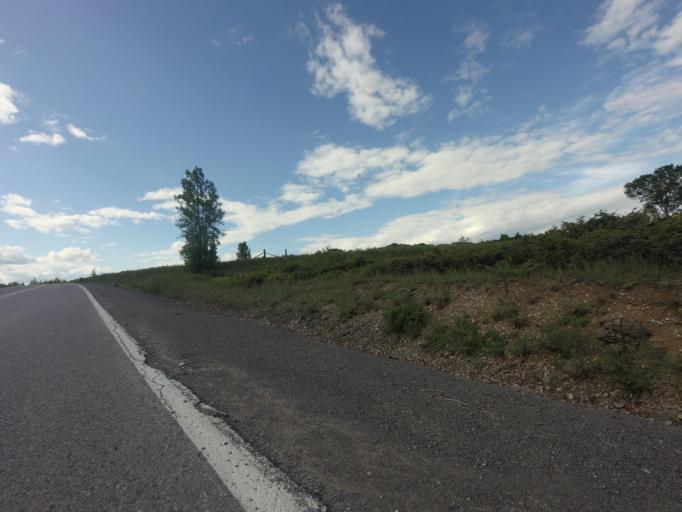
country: CA
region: Ontario
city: Arnprior
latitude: 45.3392
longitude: -76.1920
